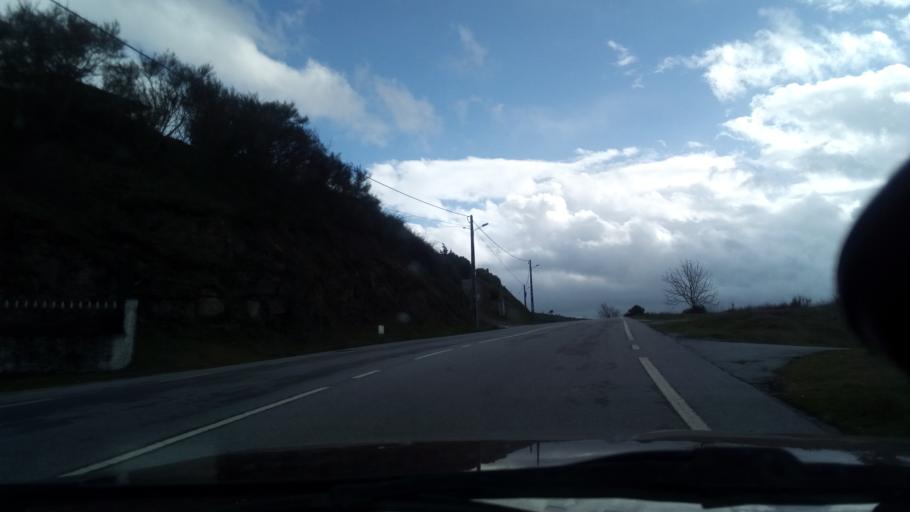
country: PT
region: Guarda
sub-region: Guarda
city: Guarda
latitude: 40.5443
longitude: -7.2976
